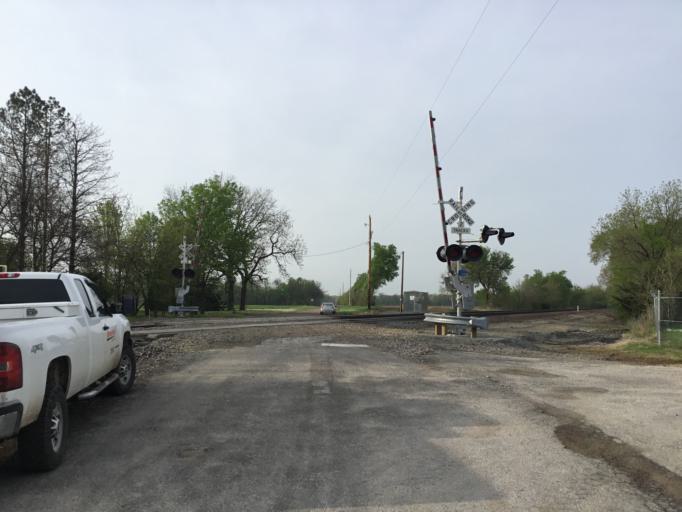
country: US
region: Kansas
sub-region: Butler County
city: El Dorado
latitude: 37.7618
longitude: -96.8894
